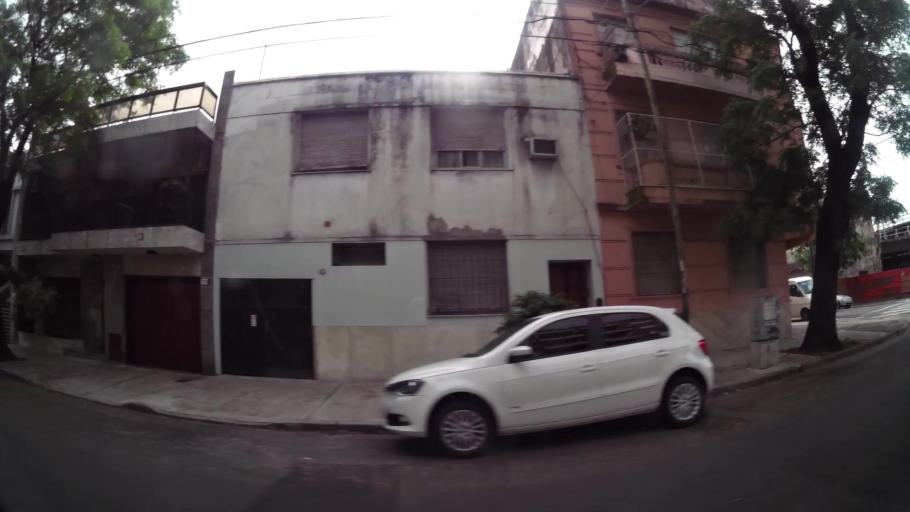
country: AR
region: Buenos Aires F.D.
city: Buenos Aires
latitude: -34.6284
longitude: -58.4183
